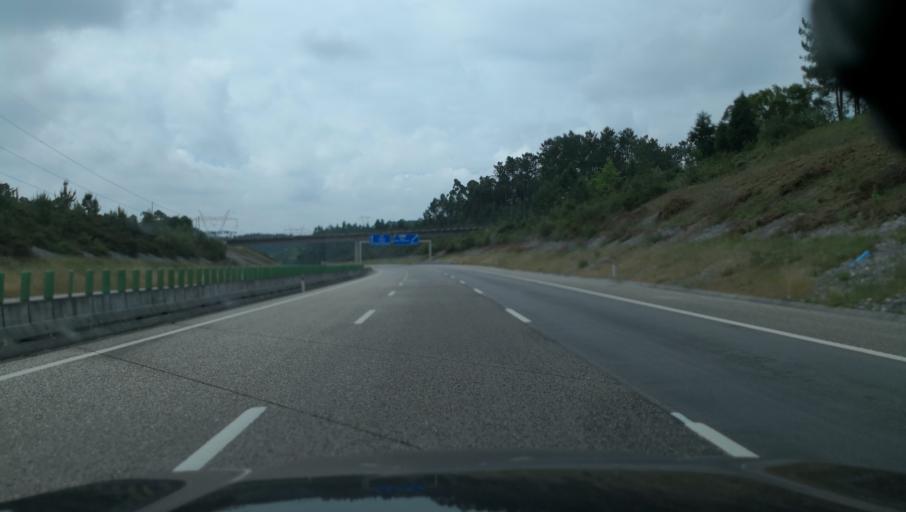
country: PT
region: Leiria
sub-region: Pombal
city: Lourical
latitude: 39.9583
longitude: -8.7748
